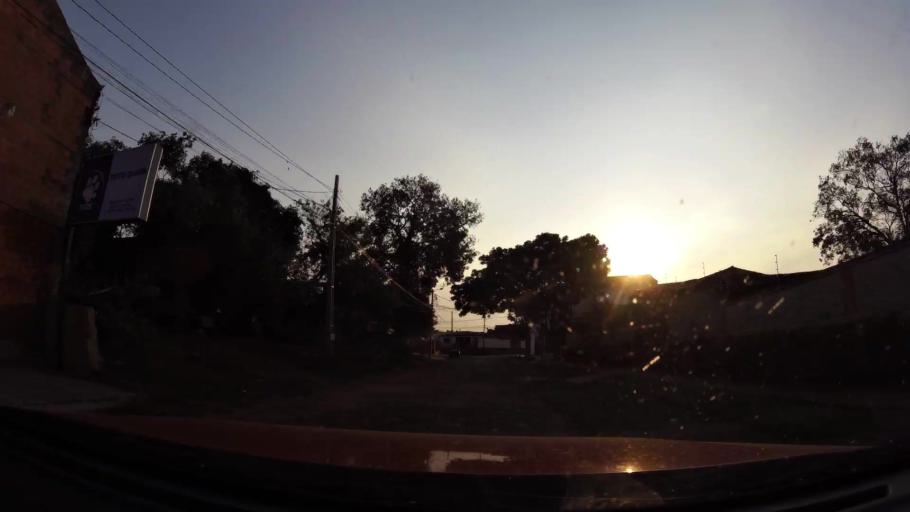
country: PY
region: Central
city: Lambare
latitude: -25.3540
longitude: -57.6014
